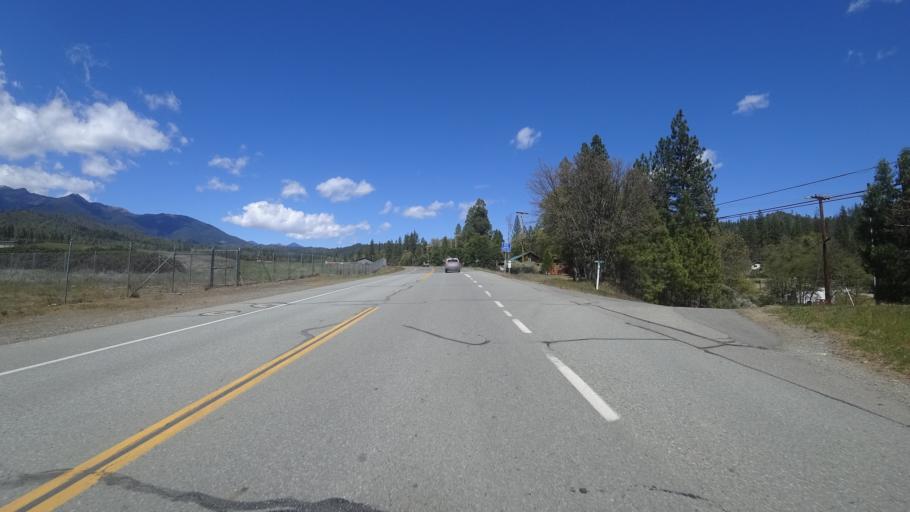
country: US
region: California
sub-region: Trinity County
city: Weaverville
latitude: 40.7421
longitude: -122.9241
